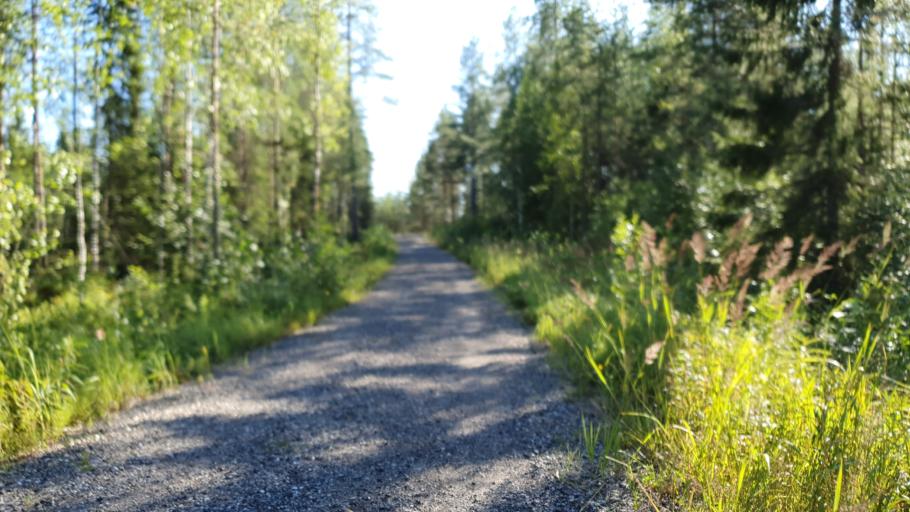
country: FI
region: Kainuu
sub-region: Kehys-Kainuu
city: Kuhmo
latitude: 64.1112
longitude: 29.5047
